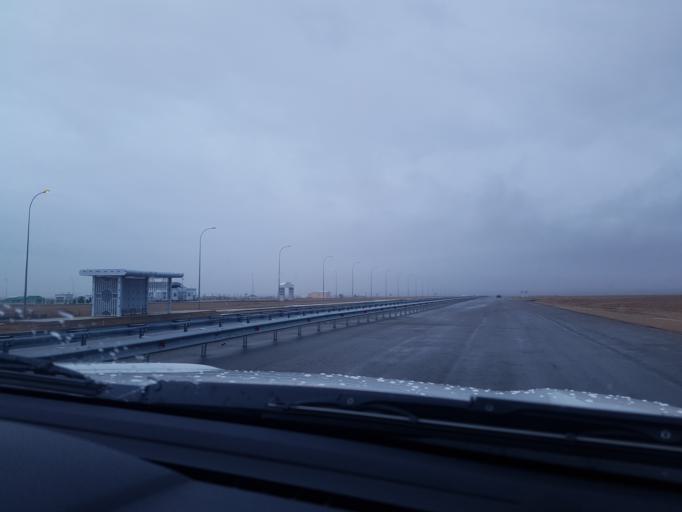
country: TM
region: Balkan
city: Balkanabat
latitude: 39.9428
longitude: 53.8495
